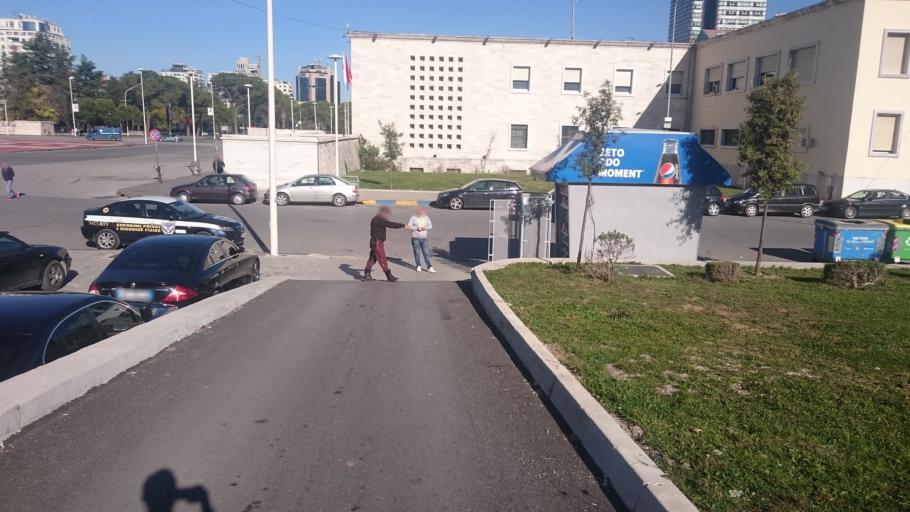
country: AL
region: Tirane
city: Tirana
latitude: 41.3173
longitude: 19.8222
